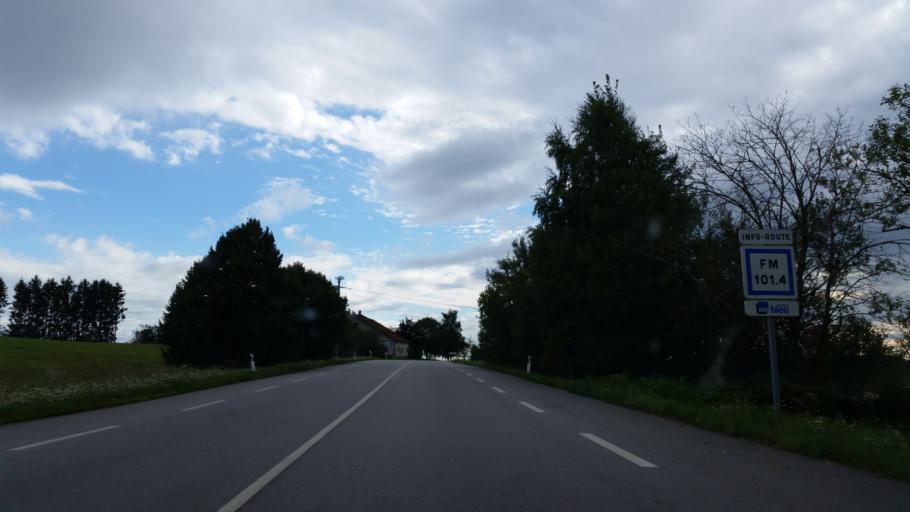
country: FR
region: Lorraine
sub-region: Departement des Vosges
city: Plombieres-les-Bains
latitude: 47.9345
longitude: 6.4460
